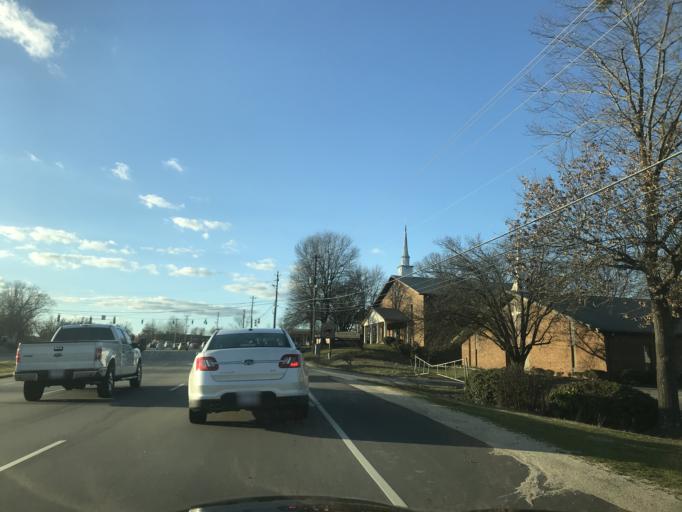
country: US
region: North Carolina
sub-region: Wake County
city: Knightdale
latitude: 35.7975
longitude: -78.5553
